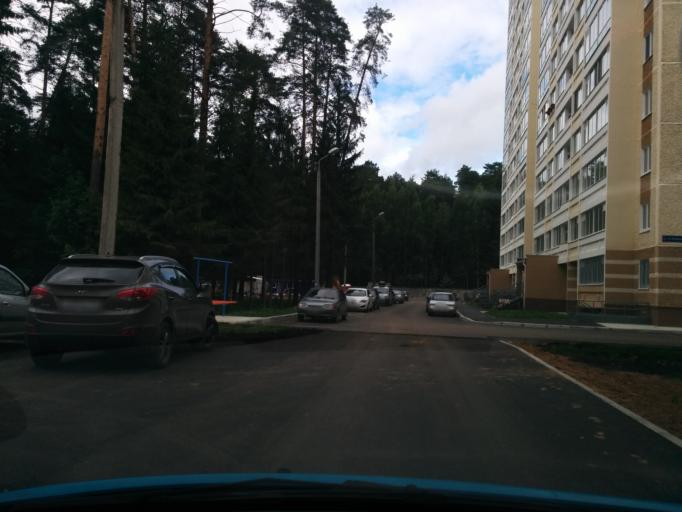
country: RU
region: Perm
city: Kondratovo
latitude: 58.0218
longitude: 56.0066
